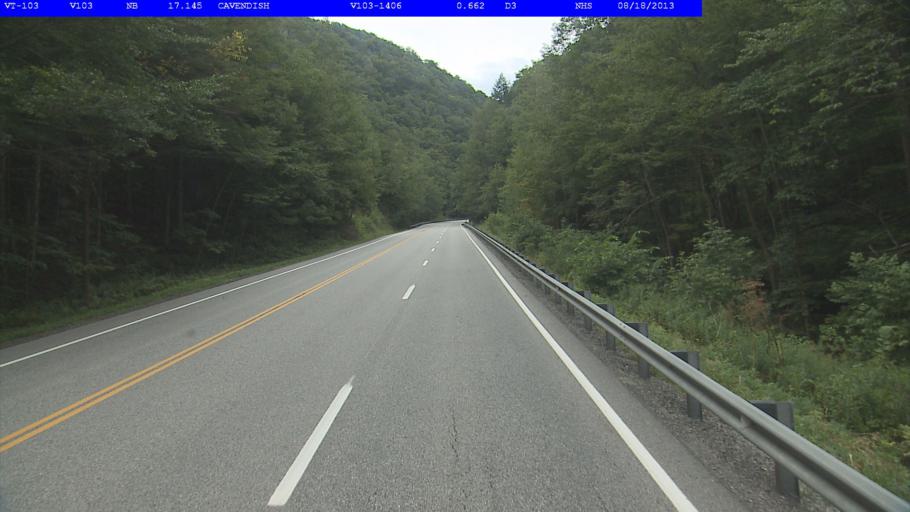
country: US
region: Vermont
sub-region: Windsor County
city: Chester
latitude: 43.3569
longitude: -72.6331
